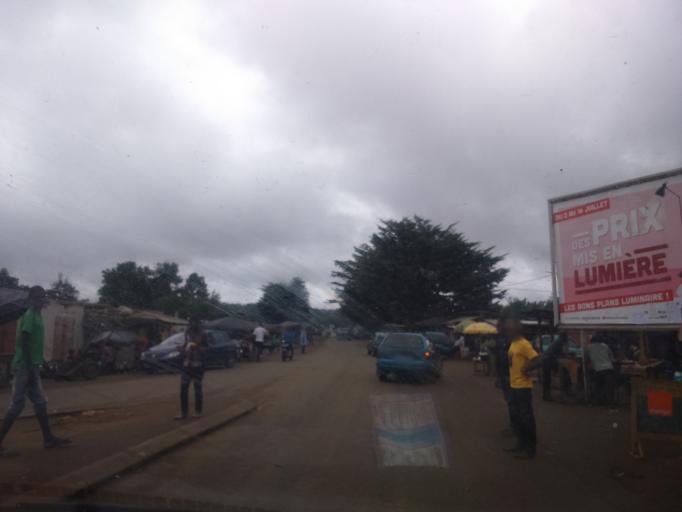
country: CI
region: Sud-Comoe
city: Bonoua
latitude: 5.2842
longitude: -3.5187
